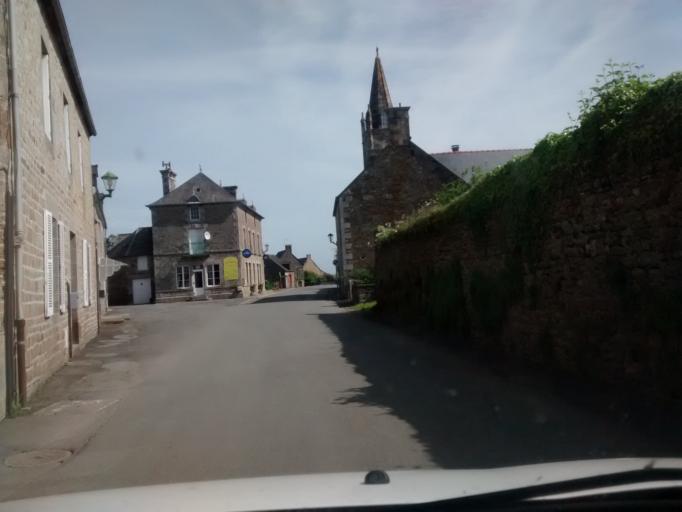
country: FR
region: Brittany
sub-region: Departement d'Ille-et-Vilaine
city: Antrain
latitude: 48.4669
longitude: -1.5038
